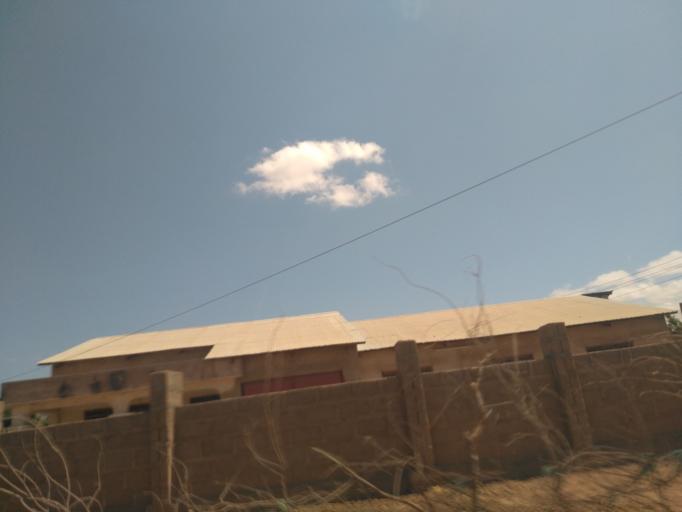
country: TZ
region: Dodoma
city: Kisasa
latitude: -6.1667
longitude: 35.7685
